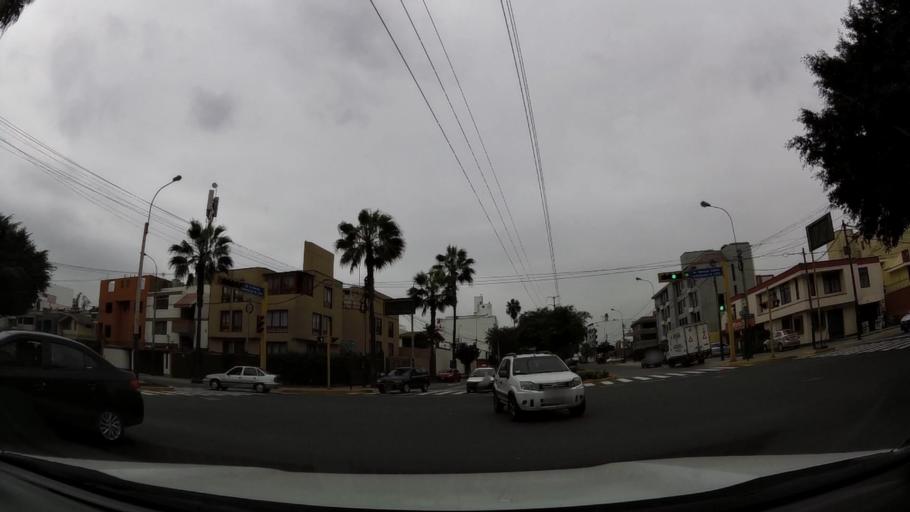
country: PE
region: Lima
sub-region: Lima
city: Surco
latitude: -12.1347
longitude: -77.0098
